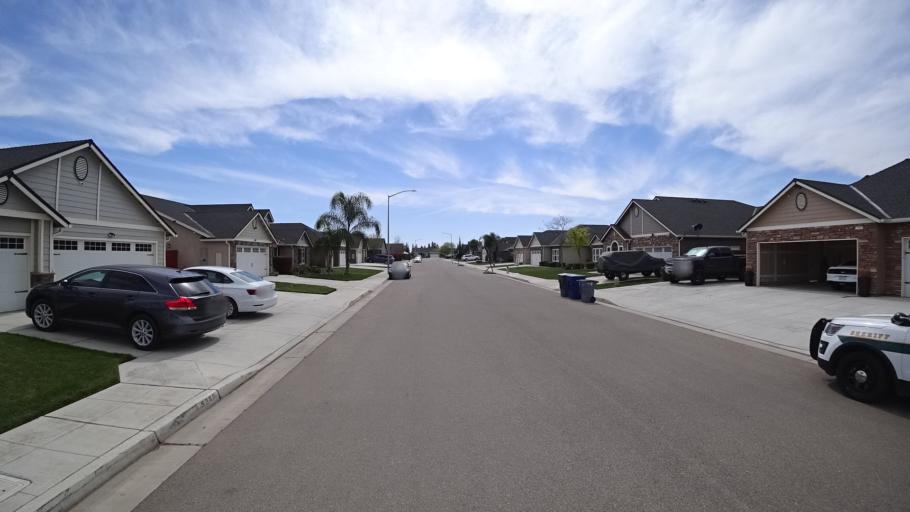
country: US
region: California
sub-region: Fresno County
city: Biola
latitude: 36.8136
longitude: -119.9226
